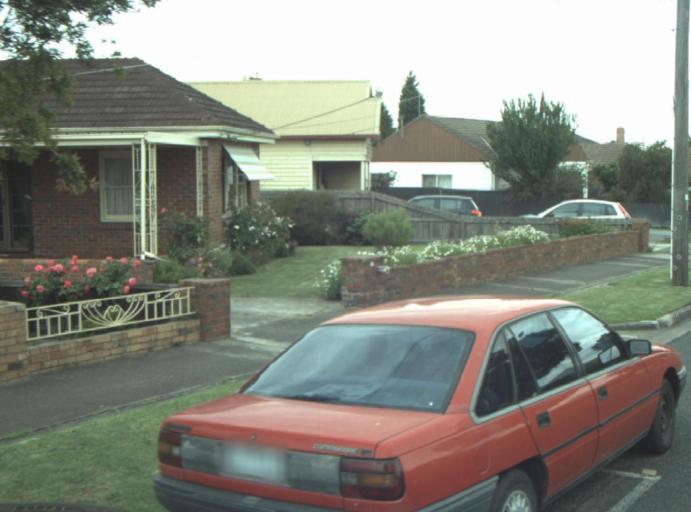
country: AU
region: Victoria
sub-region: Greater Geelong
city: East Geelong
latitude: -38.1654
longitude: 144.3728
